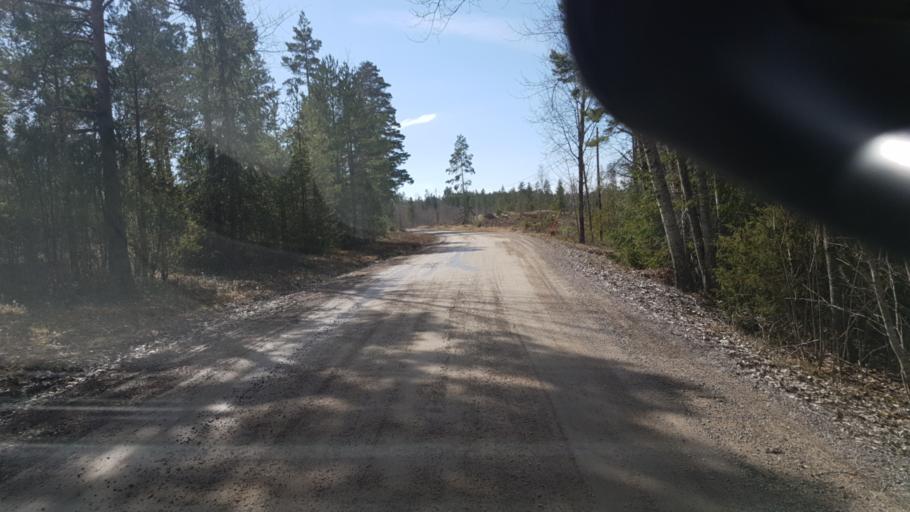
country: SE
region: Vaermland
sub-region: Arvika Kommun
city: Arvika
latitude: 59.5264
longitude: 12.7365
